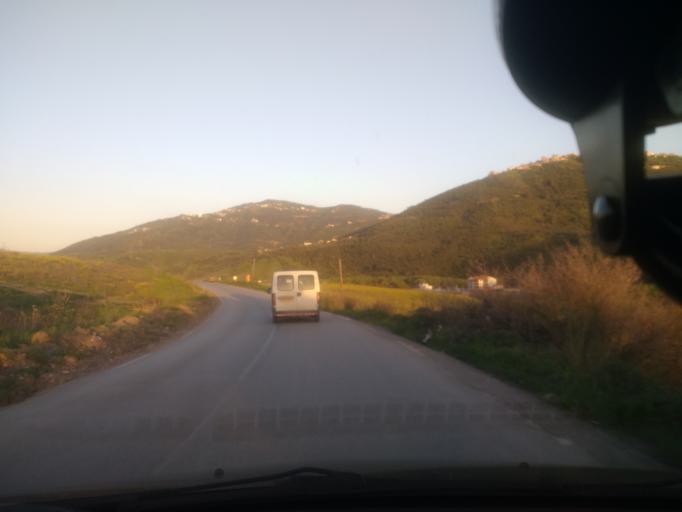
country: DZ
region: Boumerdes
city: Makouda
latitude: 36.7592
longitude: 4.0591
